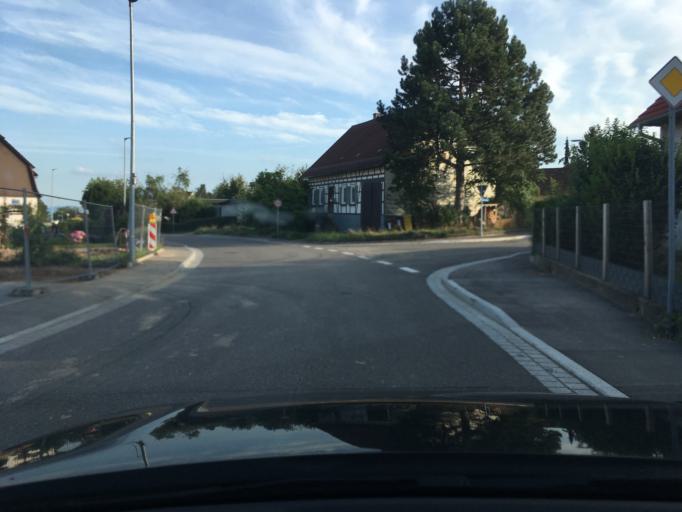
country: DE
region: Baden-Wuerttemberg
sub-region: Regierungsbezirk Stuttgart
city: Schorndorf
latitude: 48.7756
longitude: 9.5540
